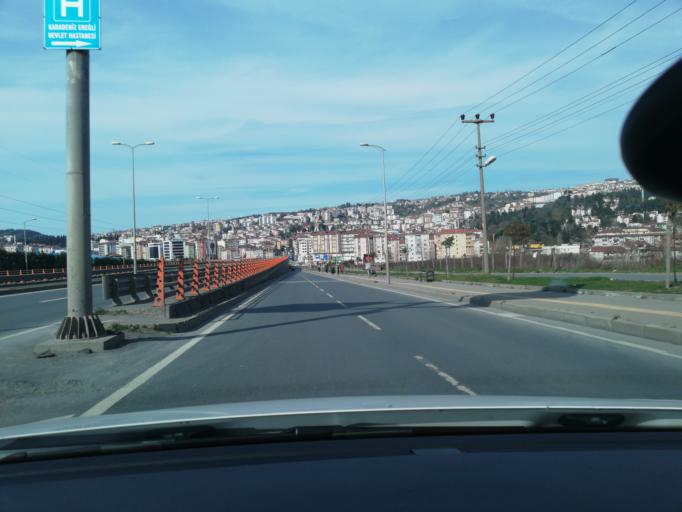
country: TR
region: Zonguldak
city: Eregli
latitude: 41.2659
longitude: 31.4353
